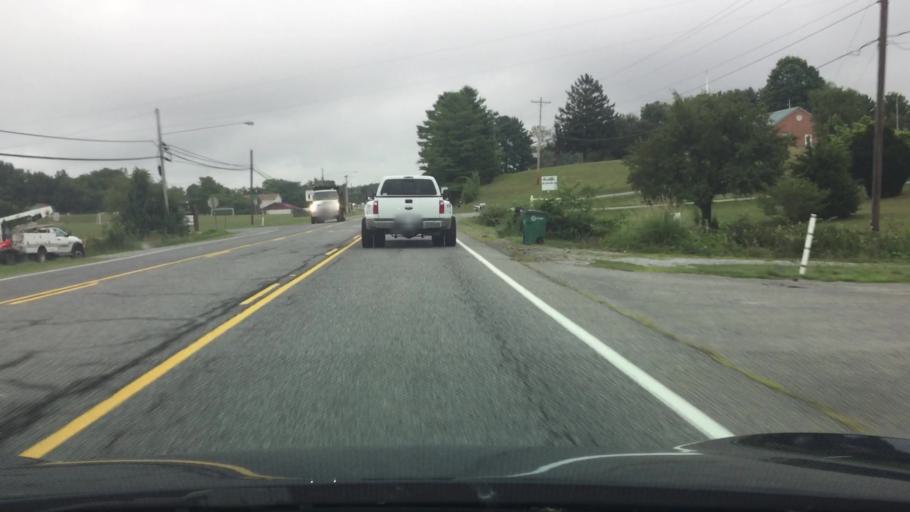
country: US
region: Virginia
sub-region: Montgomery County
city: Christiansburg
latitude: 37.1385
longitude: -80.3448
